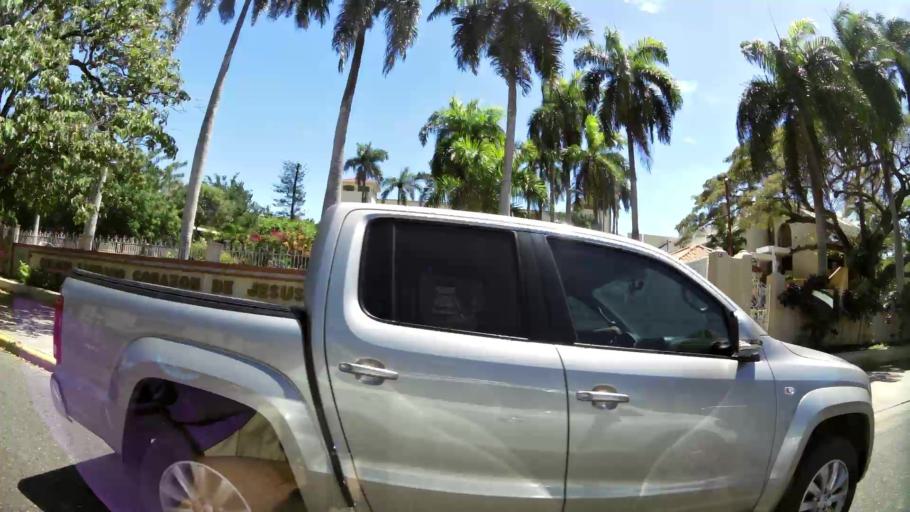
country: DO
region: Santiago
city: Santiago de los Caballeros
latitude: 19.4553
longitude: -70.6954
